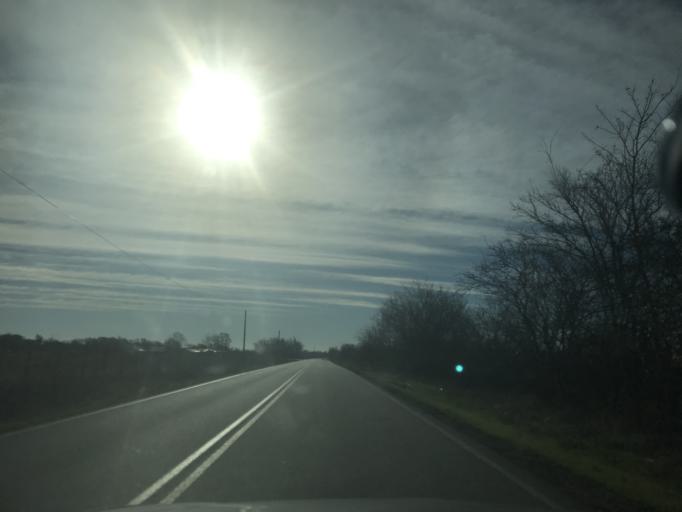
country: US
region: Texas
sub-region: Travis County
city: Manor
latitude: 30.2960
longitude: -97.5256
